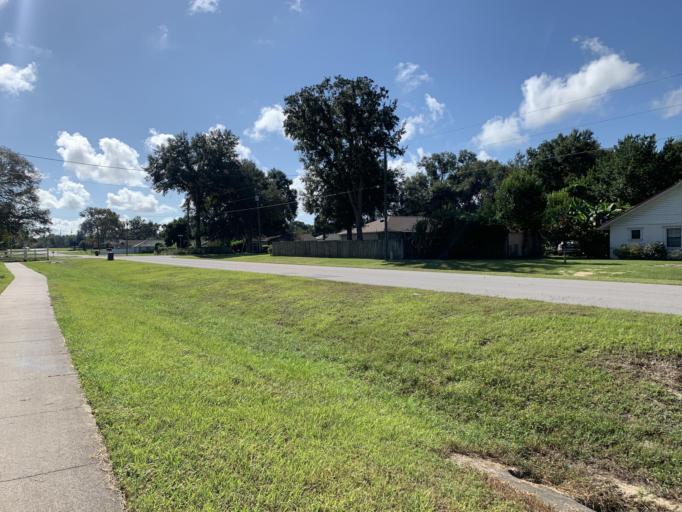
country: US
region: Florida
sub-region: Marion County
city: Silver Springs Shores
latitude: 29.1592
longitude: -82.0497
